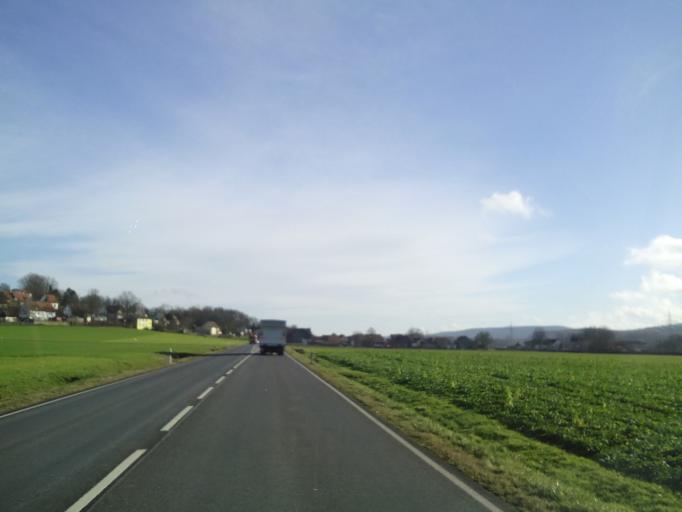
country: DE
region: Bavaria
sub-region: Upper Franconia
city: Redwitz an der Rodach
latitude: 50.1552
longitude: 11.2075
